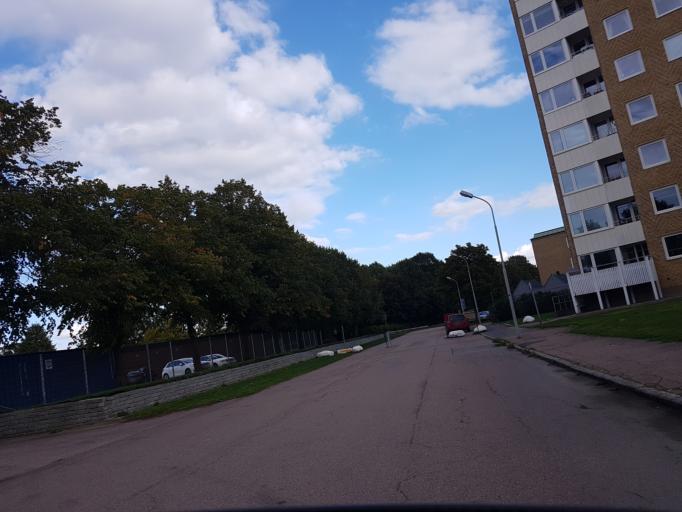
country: SE
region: Skane
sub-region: Landskrona
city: Landskrona
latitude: 55.8831
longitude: 12.8240
